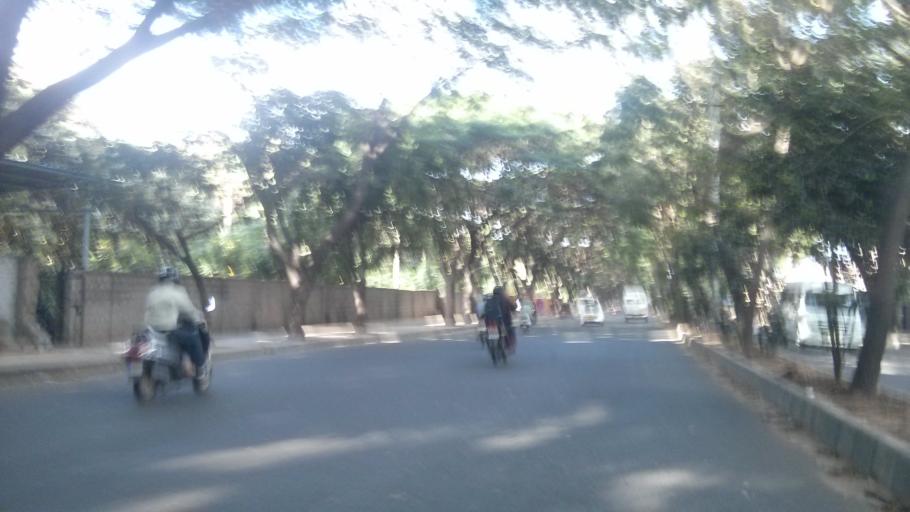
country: IN
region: Karnataka
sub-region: Bangalore Urban
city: Bangalore
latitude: 12.9546
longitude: 77.6830
